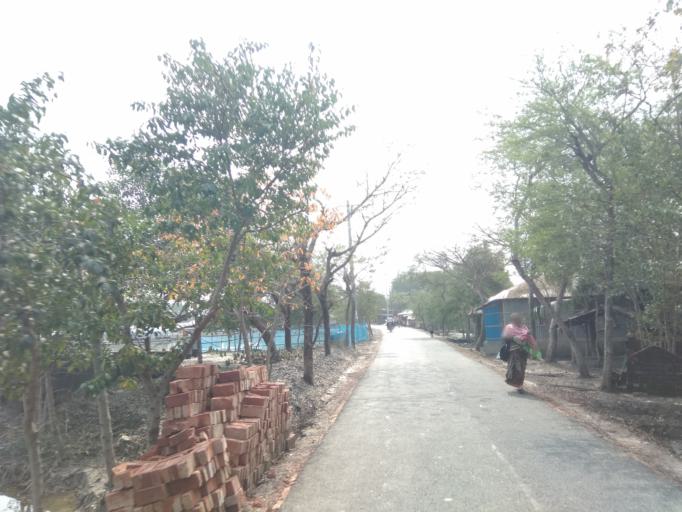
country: IN
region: West Bengal
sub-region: North 24 Parganas
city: Gosaba
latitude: 22.2658
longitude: 89.2184
